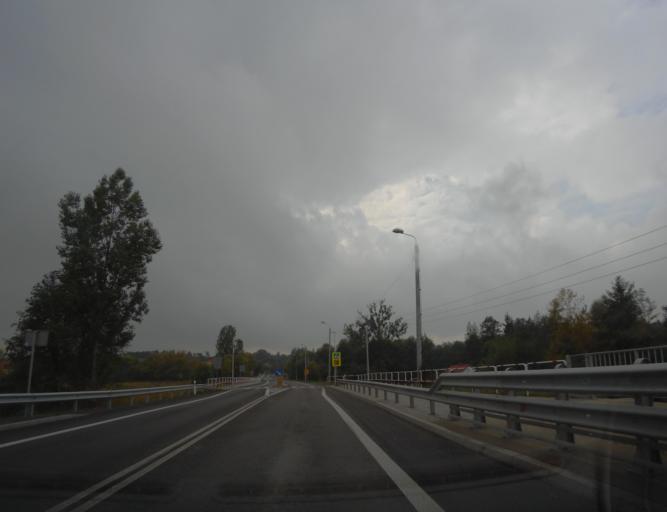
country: PL
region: Lublin Voivodeship
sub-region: Powiat krasnostawski
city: Krasnystaw
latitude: 51.0156
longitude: 23.1931
